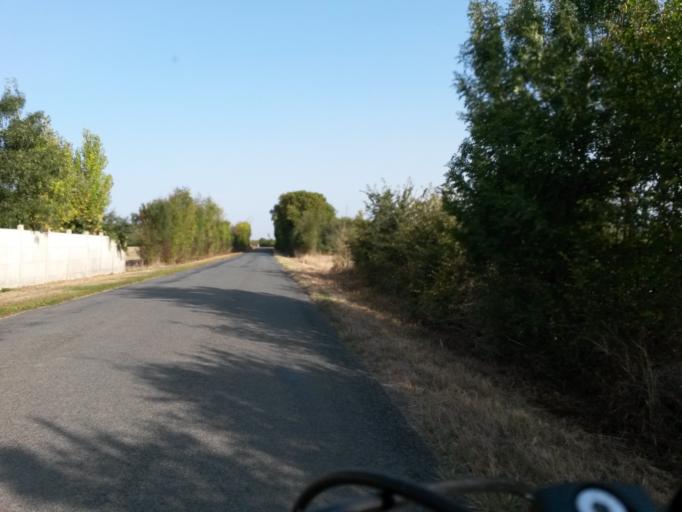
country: FR
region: Poitou-Charentes
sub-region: Departement de la Charente-Maritime
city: Saint-Xandre
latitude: 46.2198
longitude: -1.1050
